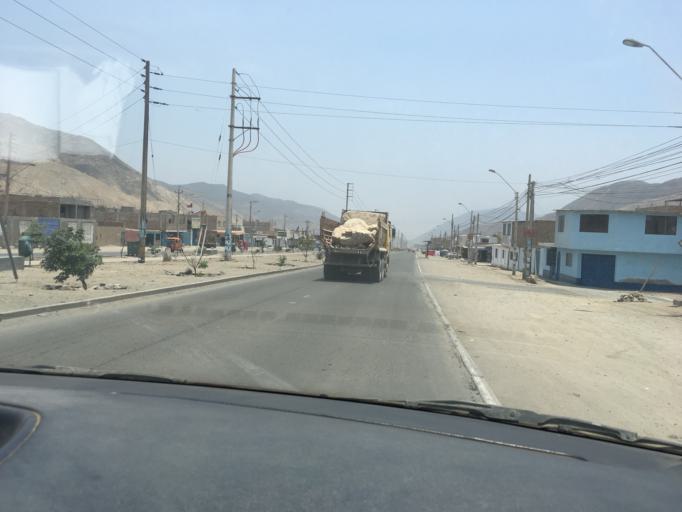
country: PE
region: Lima
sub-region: Lima
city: Cieneguilla
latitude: -12.1151
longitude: -76.8734
